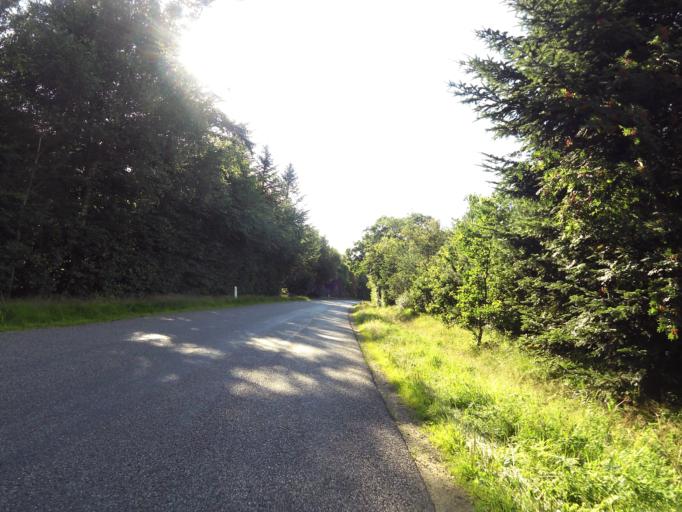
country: DK
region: South Denmark
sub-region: Haderslev Kommune
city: Vojens
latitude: 55.2111
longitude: 9.2403
